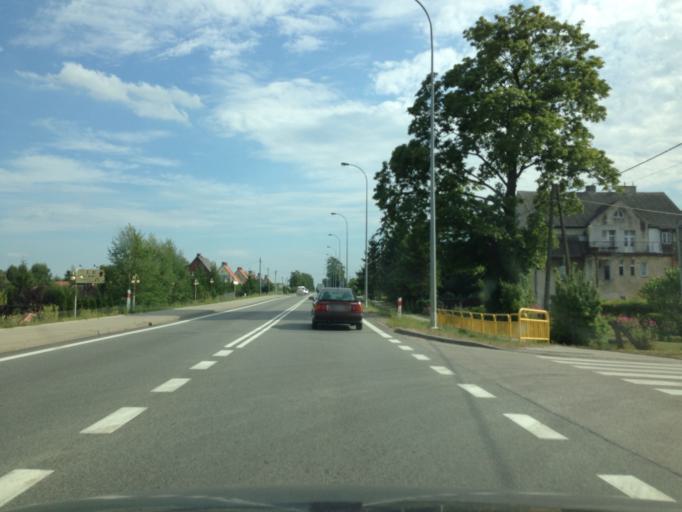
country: PL
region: Pomeranian Voivodeship
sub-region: Powiat gdanski
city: Pszczolki
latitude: 54.1715
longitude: 18.6994
